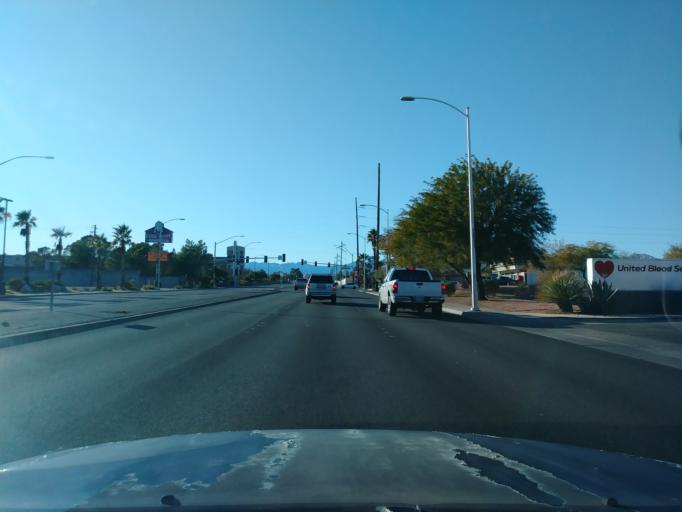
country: US
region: Nevada
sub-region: Clark County
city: Spring Valley
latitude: 36.1592
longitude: -115.2495
